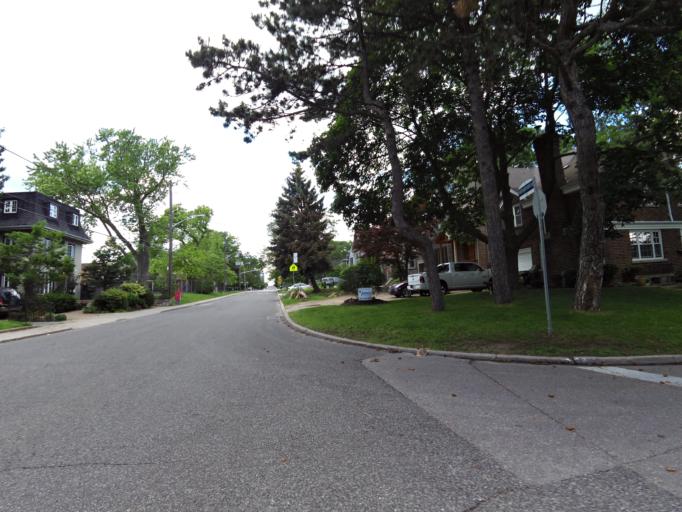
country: CA
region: Ontario
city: Scarborough
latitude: 43.6784
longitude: -79.2776
